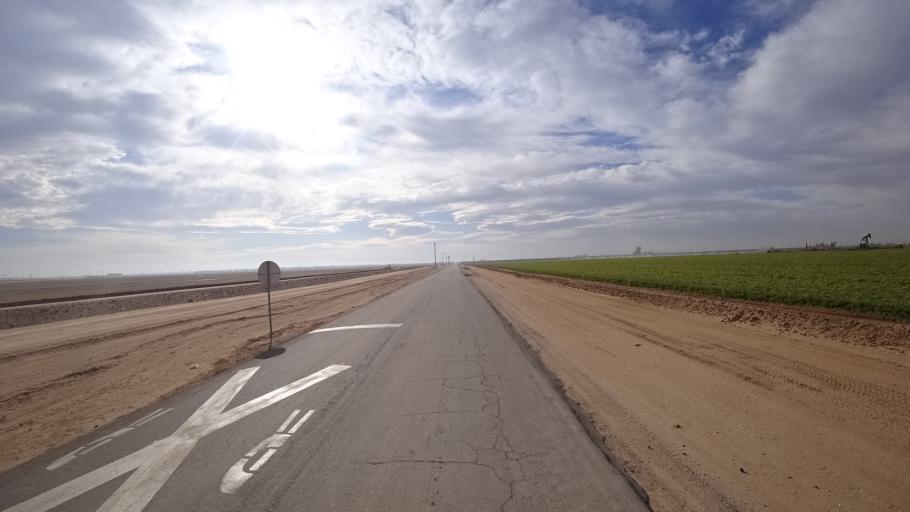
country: US
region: California
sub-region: Kern County
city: Rosedale
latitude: 35.4179
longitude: -119.1721
